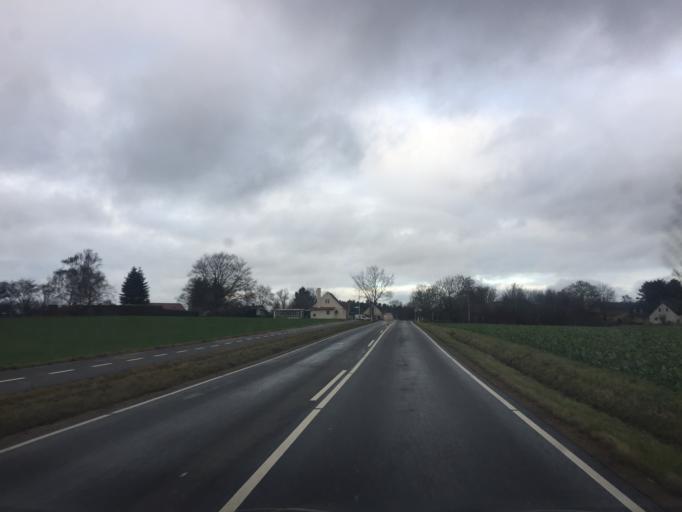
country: DK
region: Zealand
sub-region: Holbaek Kommune
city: Tollose
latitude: 55.6056
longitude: 11.7064
